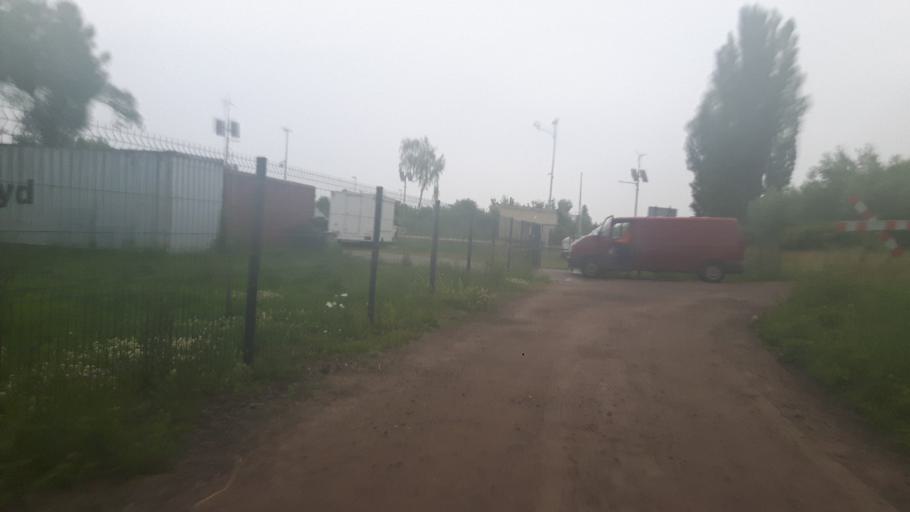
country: PL
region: Pomeranian Voivodeship
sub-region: Powiat nowodworski
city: Krynica Morska
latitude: 54.2786
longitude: 19.4253
